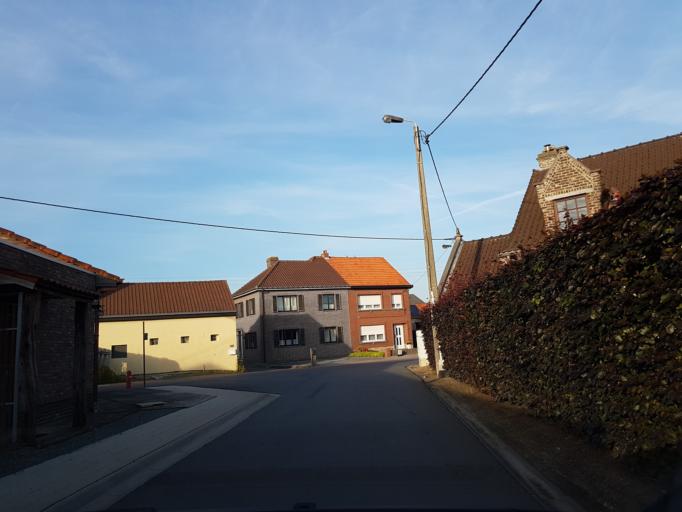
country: BE
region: Flanders
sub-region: Provincie Vlaams-Brabant
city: Opwijk
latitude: 50.9790
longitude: 4.2099
